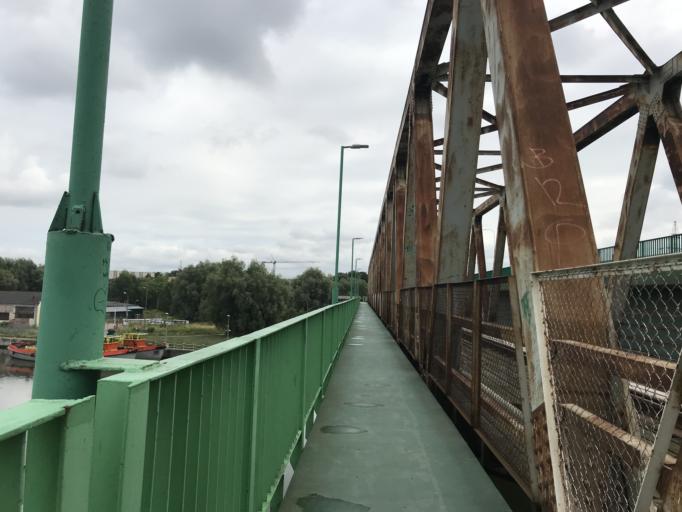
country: PL
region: Warmian-Masurian Voivodeship
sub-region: Powiat elblaski
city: Elblag
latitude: 54.1731
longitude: 19.3877
